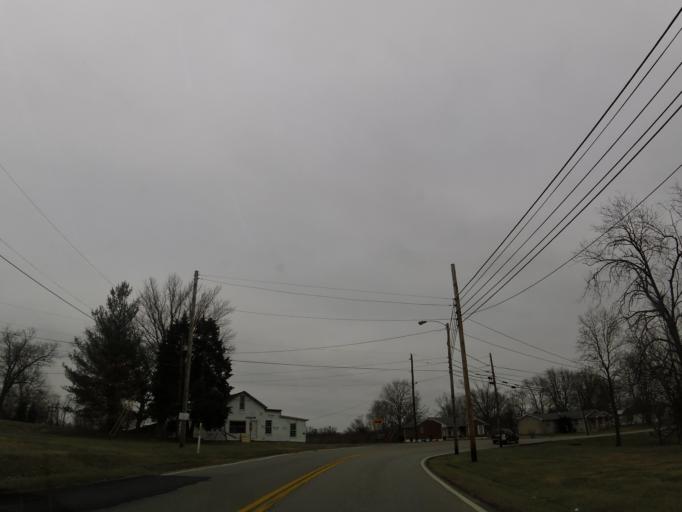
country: US
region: Kentucky
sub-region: Trimble County
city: Providence
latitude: 38.5246
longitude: -85.2178
